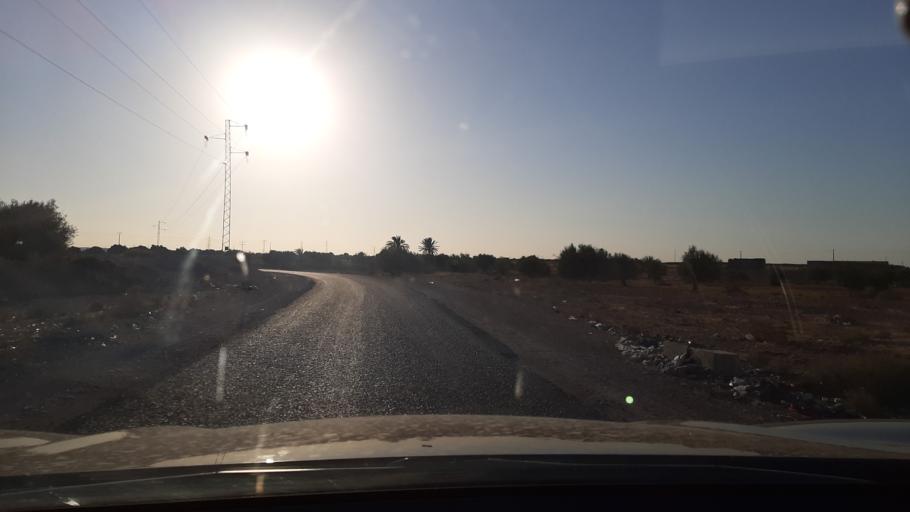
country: TN
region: Qabis
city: Matmata
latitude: 33.6164
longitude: 10.2446
